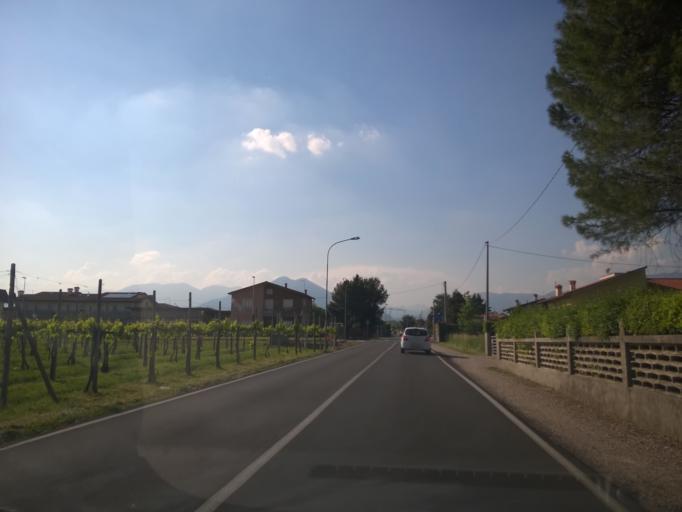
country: IT
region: Veneto
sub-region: Provincia di Vicenza
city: Thiene
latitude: 45.6967
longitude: 11.4934
